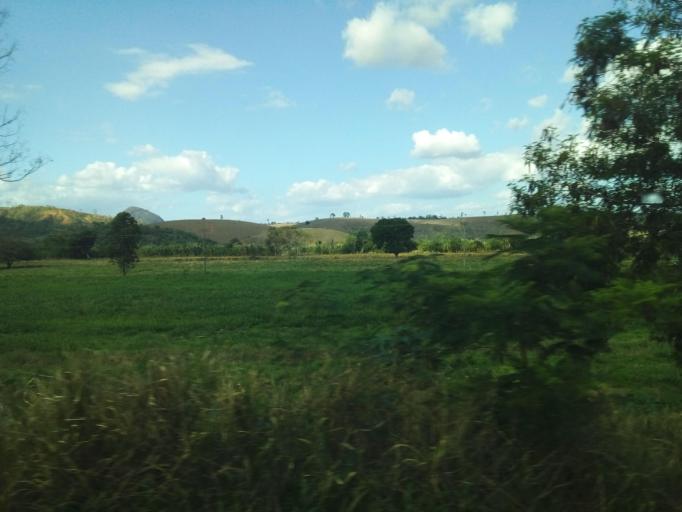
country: BR
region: Minas Gerais
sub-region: Conselheiro Pena
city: Conselheiro Pena
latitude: -18.9889
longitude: -41.5993
